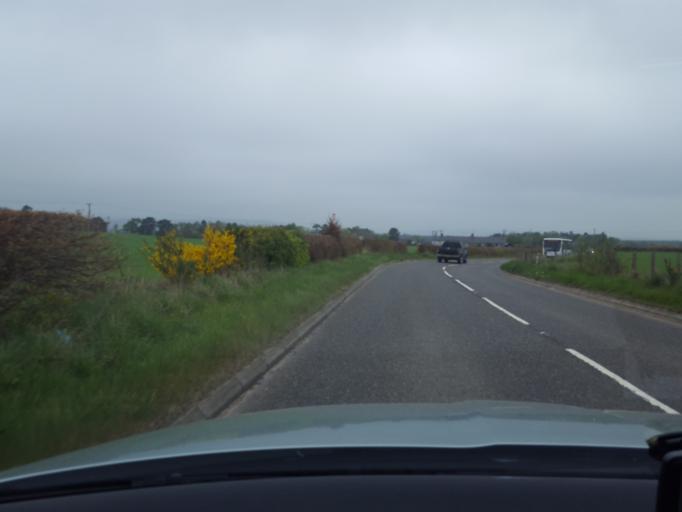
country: GB
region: Scotland
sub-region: Angus
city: Brechin
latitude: 56.7757
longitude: -2.6443
